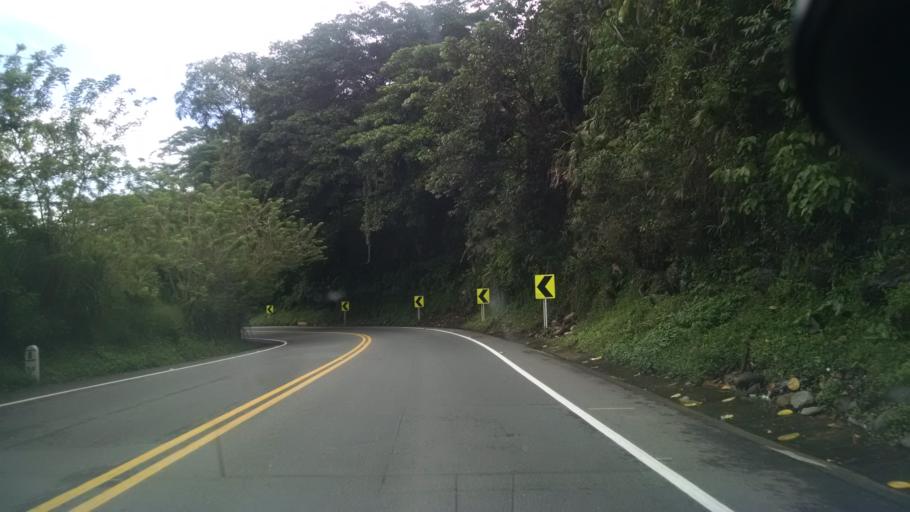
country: CO
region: Caldas
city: Palestina
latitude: 5.0530
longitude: -75.6047
